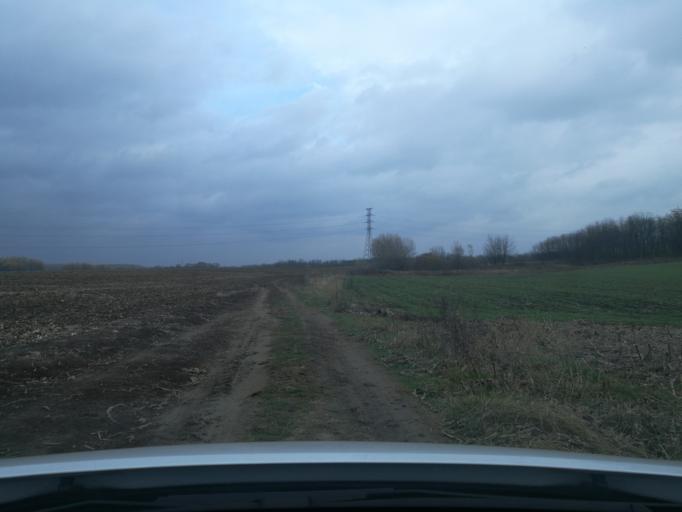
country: HU
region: Szabolcs-Szatmar-Bereg
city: Nyirpazony
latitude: 47.9634
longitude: 21.7843
